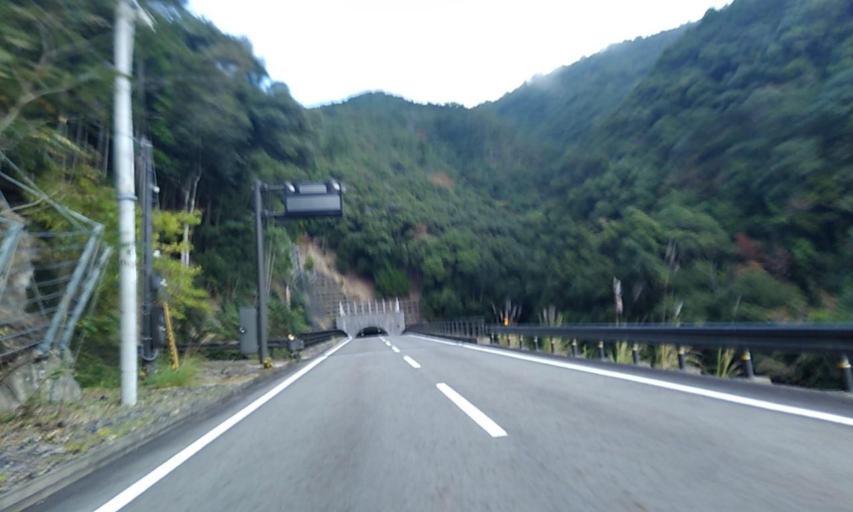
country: JP
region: Wakayama
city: Shingu
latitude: 33.8795
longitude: 135.8767
